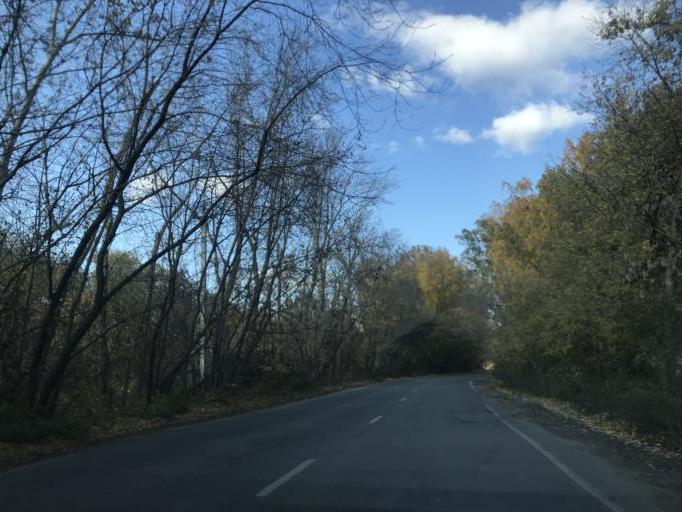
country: RU
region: Chelyabinsk
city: Dolgoderevenskoye
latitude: 55.2589
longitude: 61.3635
